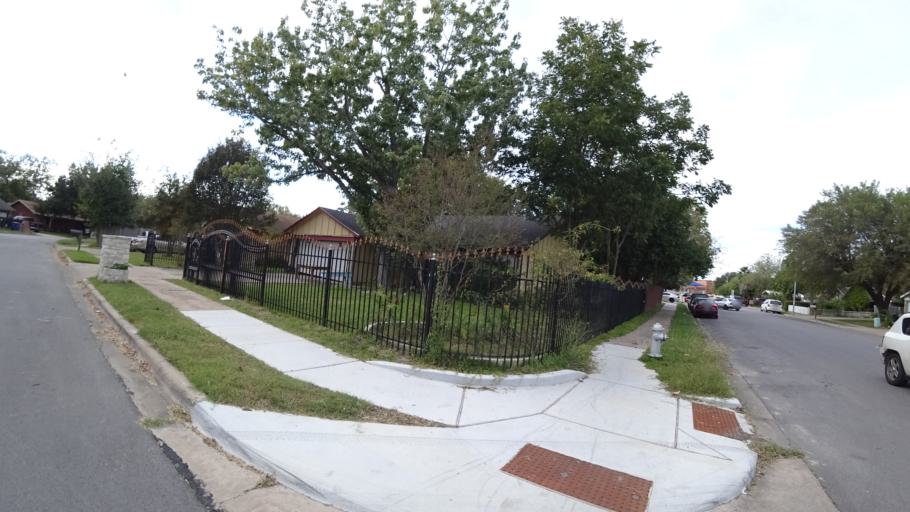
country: US
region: Texas
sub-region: Travis County
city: Onion Creek
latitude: 30.1944
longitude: -97.7539
